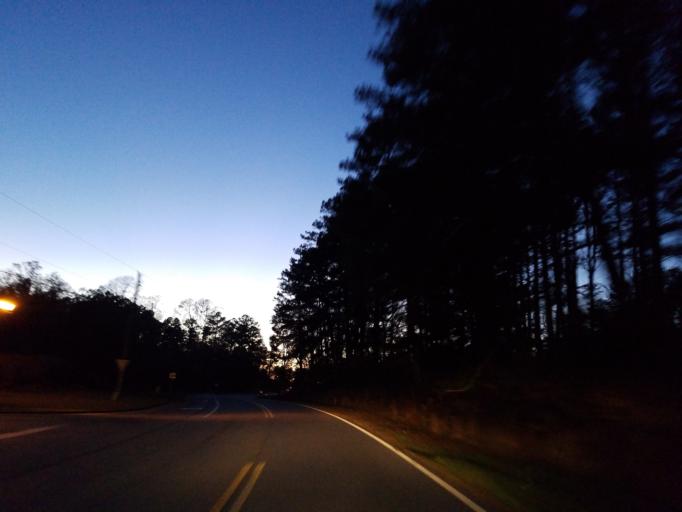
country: US
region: Georgia
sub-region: Dawson County
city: Dawsonville
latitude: 34.3329
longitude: -84.1020
